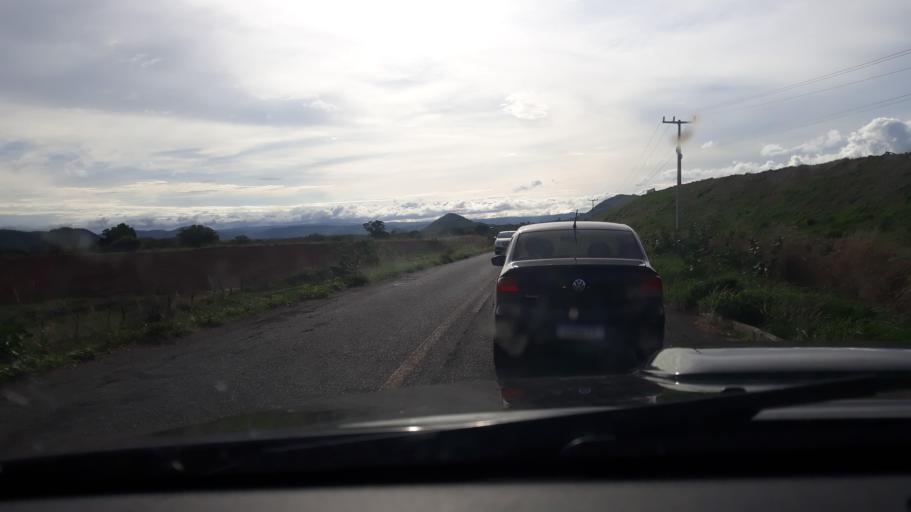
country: BR
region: Bahia
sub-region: Guanambi
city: Guanambi
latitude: -14.1472
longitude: -42.8326
